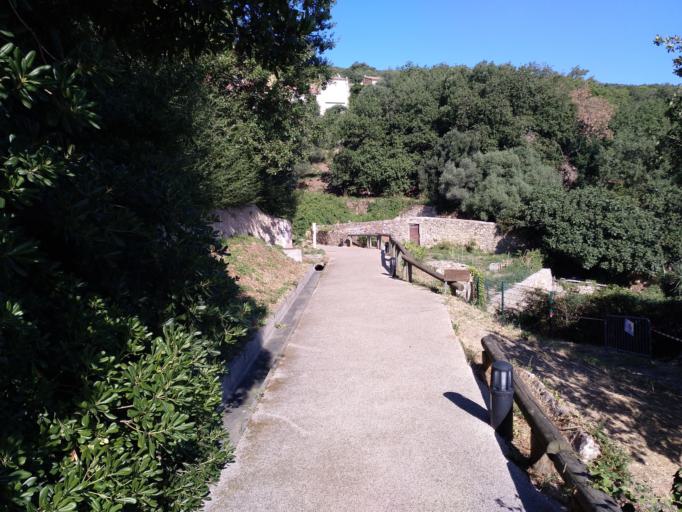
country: FR
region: Provence-Alpes-Cote d'Azur
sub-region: Departement du Var
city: Ramatuelle
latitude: 43.2160
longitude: 6.6132
